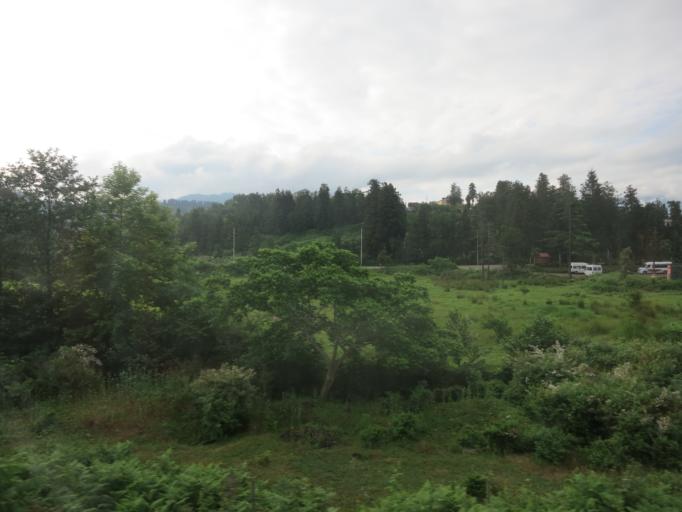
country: GE
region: Ajaria
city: Kobuleti
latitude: 41.7458
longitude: 41.7390
